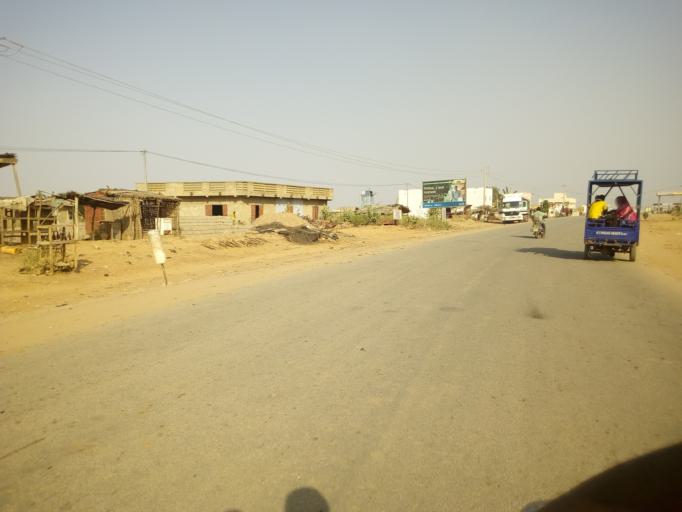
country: ML
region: Kayes
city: Kayes
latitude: 14.4635
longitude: -11.4163
